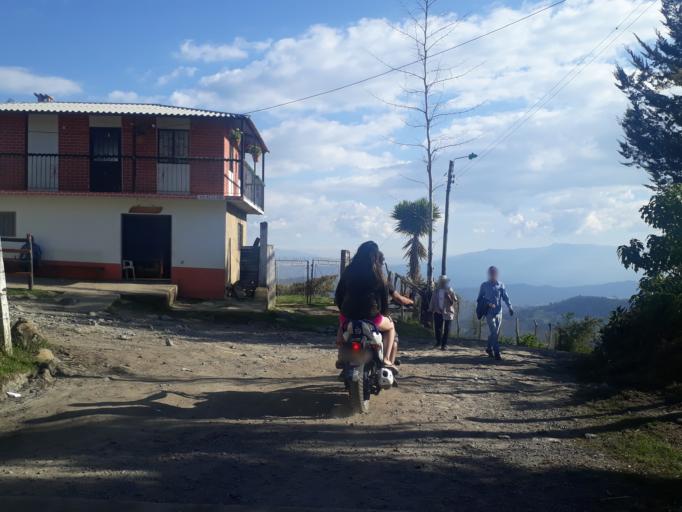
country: CO
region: Santander
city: Velez
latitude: 6.0288
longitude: -73.6666
